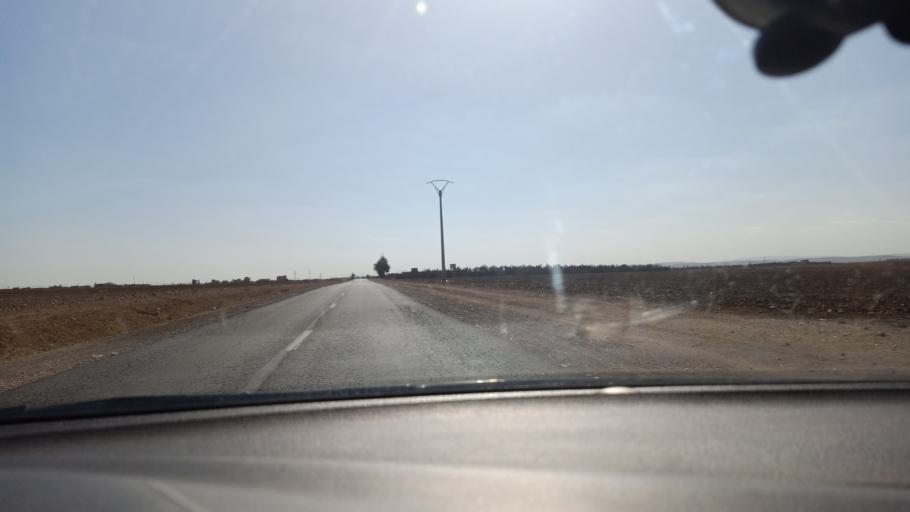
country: MA
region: Doukkala-Abda
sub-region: Safi
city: Youssoufia
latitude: 32.1253
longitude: -8.6019
